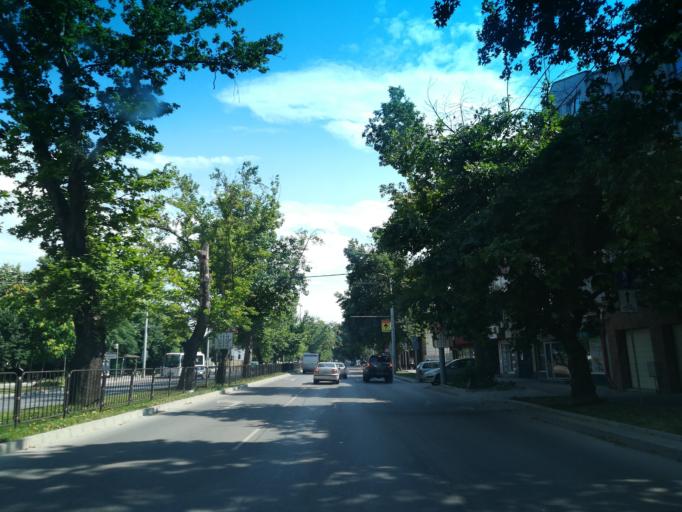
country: BG
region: Plovdiv
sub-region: Obshtina Plovdiv
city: Plovdiv
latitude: 42.1421
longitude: 24.7630
